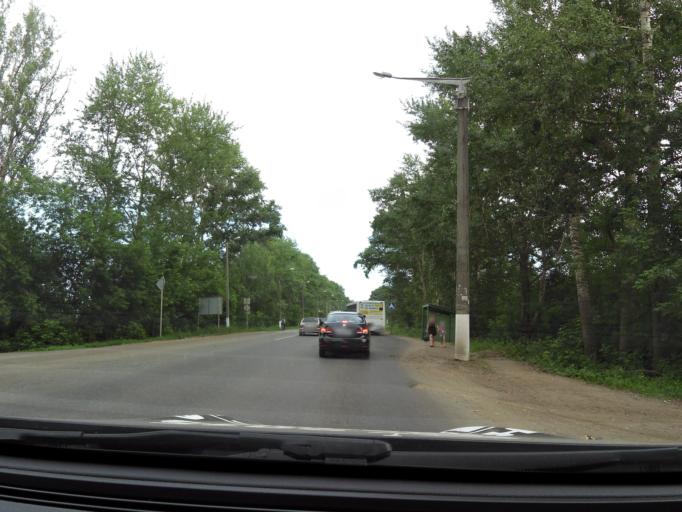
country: RU
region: Kirov
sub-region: Kirovo-Chepetskiy Rayon
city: Kirov
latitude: 58.6185
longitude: 49.7099
